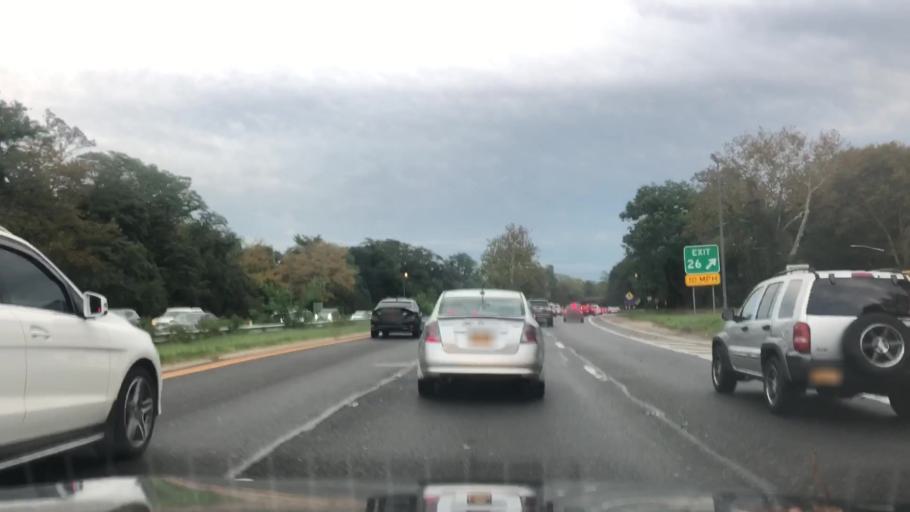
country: US
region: New York
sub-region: Nassau County
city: North Bellmore
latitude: 40.6972
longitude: -73.5366
